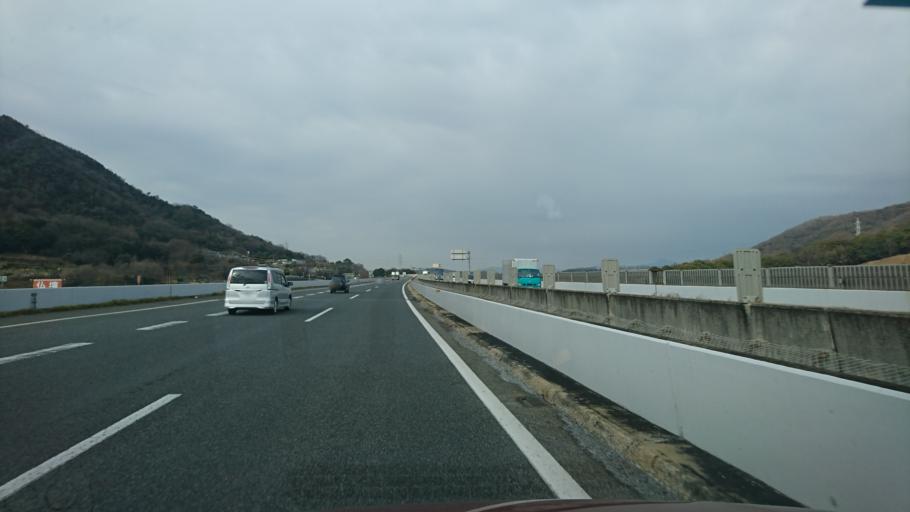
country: JP
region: Hiroshima
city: Fukuyama
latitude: 34.5143
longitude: 133.3929
